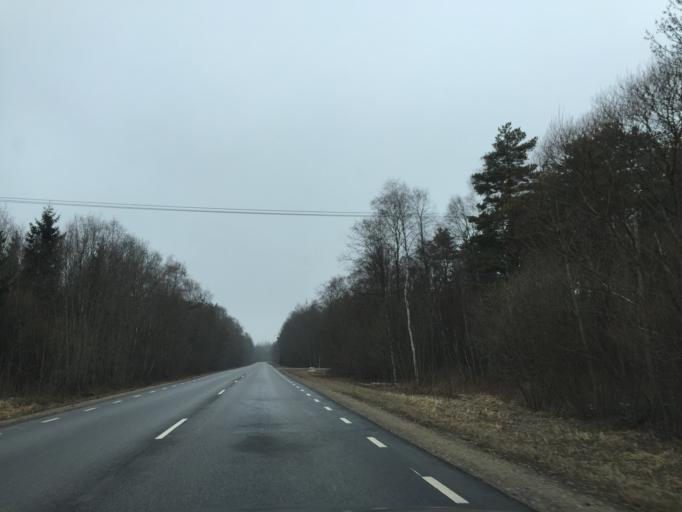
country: EE
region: Laeaene
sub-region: Lihula vald
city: Lihula
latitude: 58.6027
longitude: 23.6988
